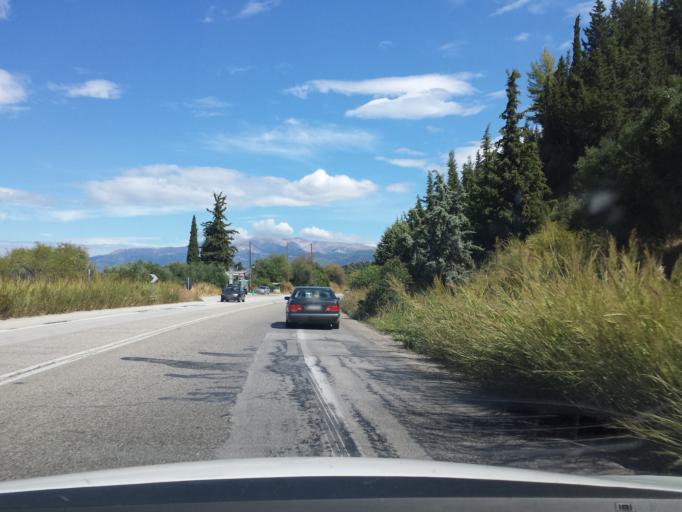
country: GR
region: West Greece
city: Vrachnaiika
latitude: 38.1545
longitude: 21.6351
